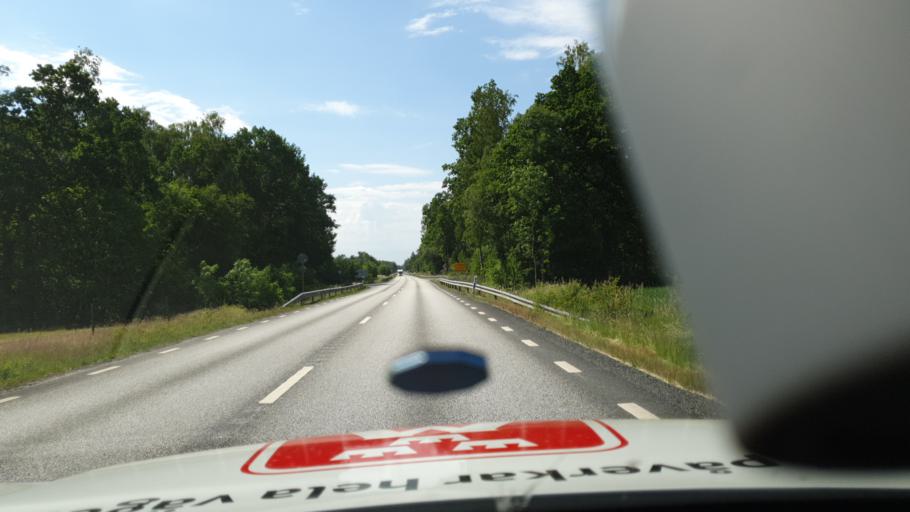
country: SE
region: Joenkoeping
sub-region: Habo Kommun
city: Habo
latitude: 58.0522
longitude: 14.1866
